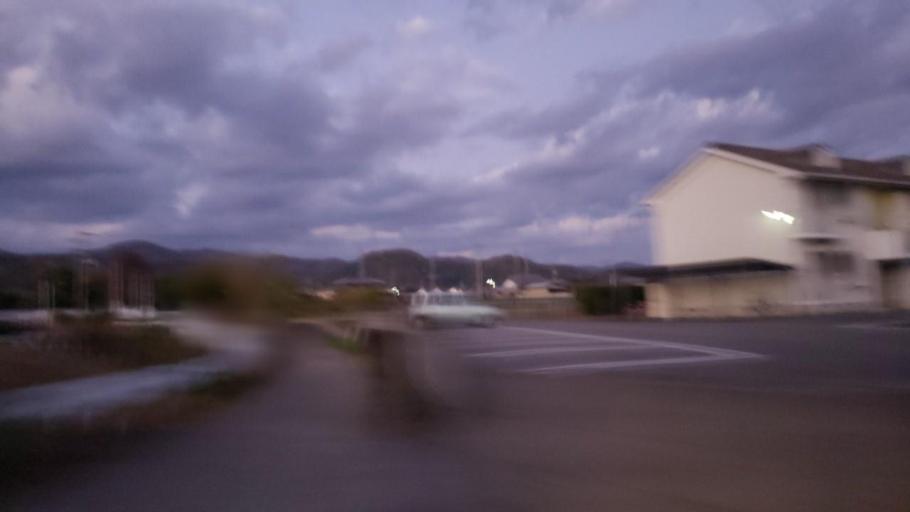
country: JP
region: Tokushima
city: Kamojimacho-jogejima
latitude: 34.0884
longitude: 134.2901
